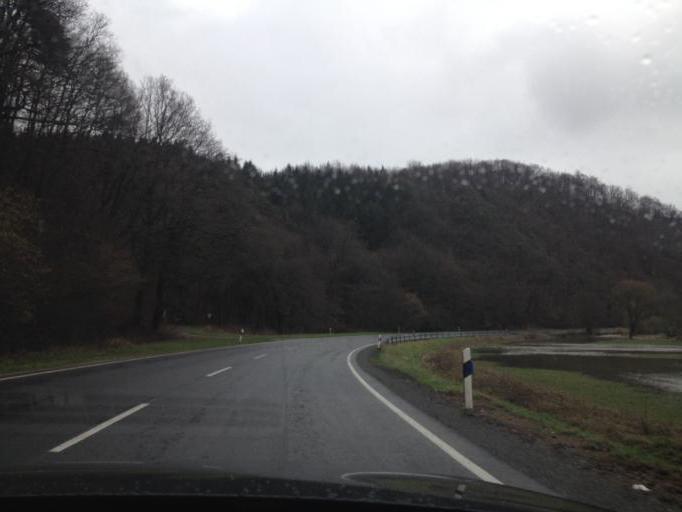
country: DE
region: Saarland
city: Nohfelden
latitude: 49.5943
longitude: 7.1375
